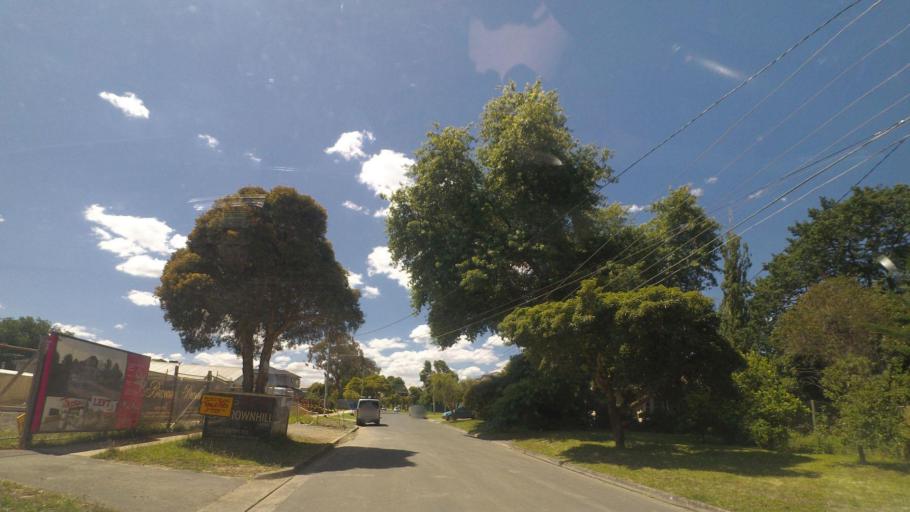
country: AU
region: Victoria
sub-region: Yarra Ranges
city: Kilsyth
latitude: -37.8053
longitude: 145.3123
